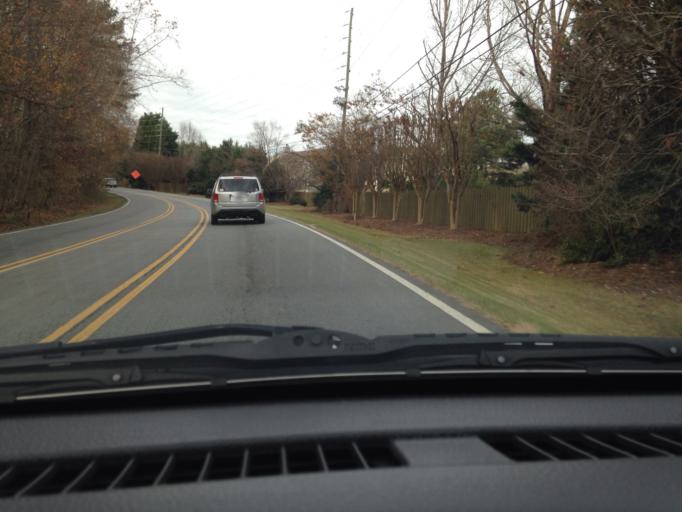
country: US
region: Georgia
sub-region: Fulton County
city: Johns Creek
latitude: 34.0816
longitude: -84.1851
